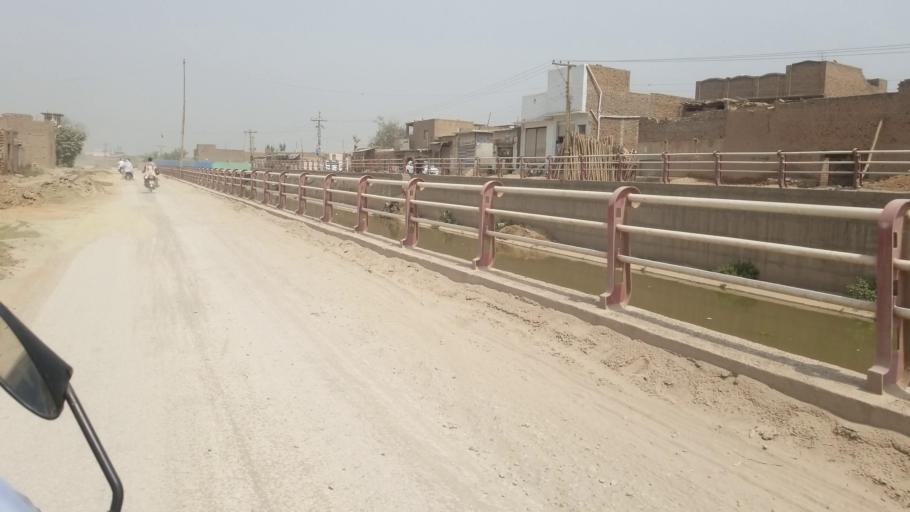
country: PK
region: Khyber Pakhtunkhwa
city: Peshawar
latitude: 33.9647
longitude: 71.5418
